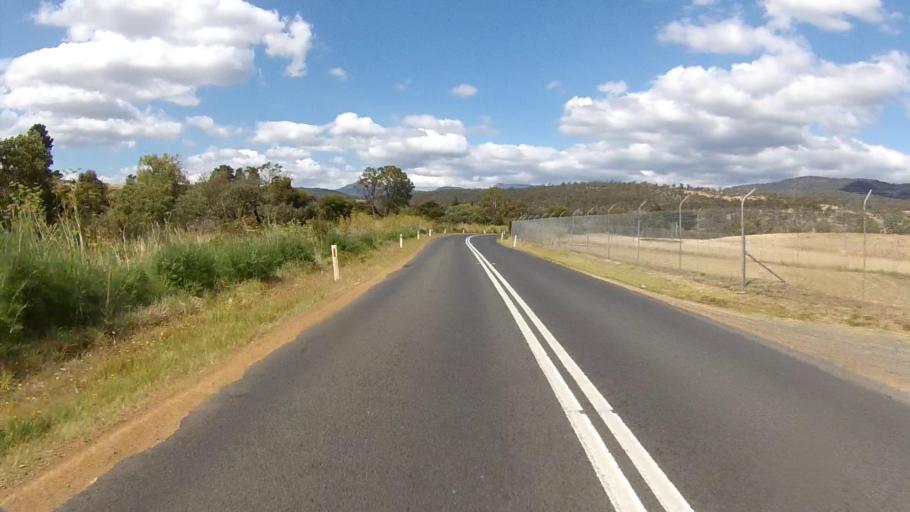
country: AU
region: Tasmania
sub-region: Derwent Valley
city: New Norfolk
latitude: -42.7693
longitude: 147.0254
